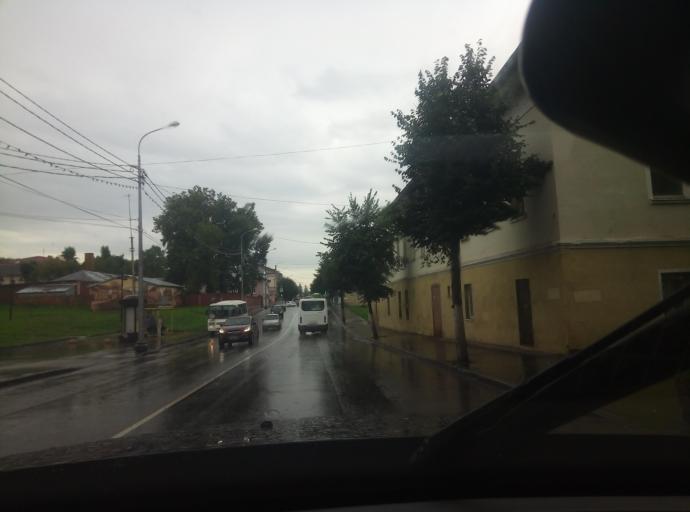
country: RU
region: Moskovskaya
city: Serpukhov
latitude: 54.9168
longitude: 37.4126
